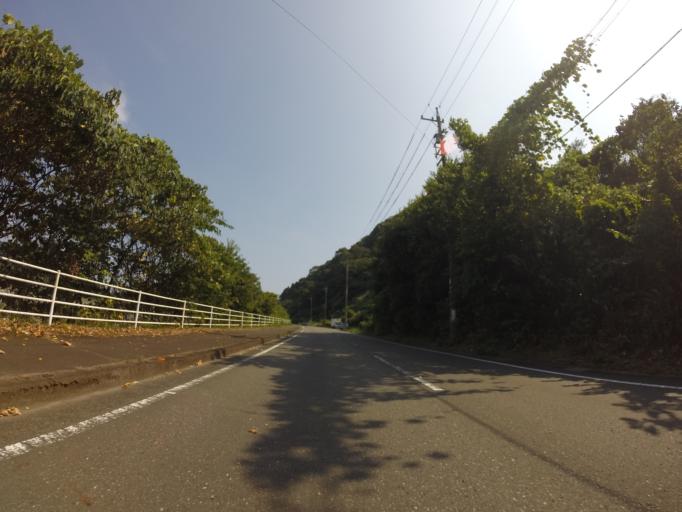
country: JP
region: Shizuoka
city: Shizuoka-shi
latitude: 35.0565
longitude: 138.3638
